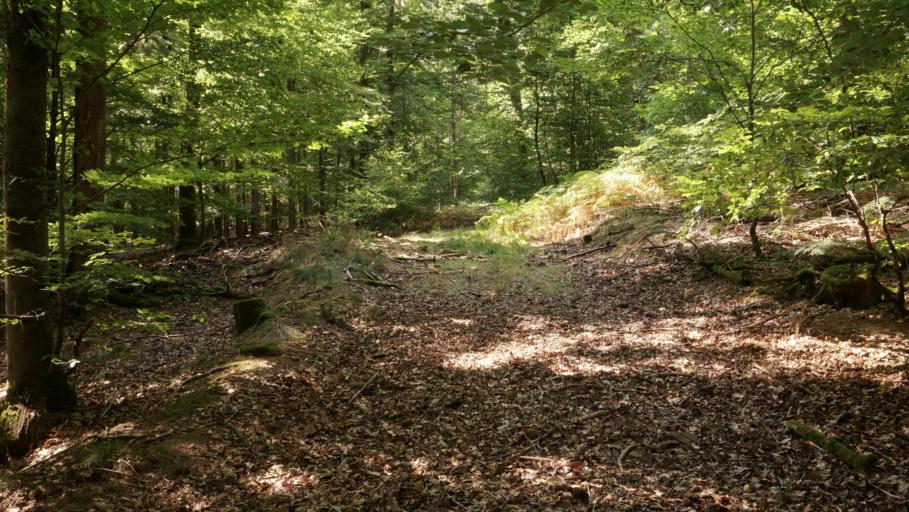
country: DE
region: Baden-Wuerttemberg
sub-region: Karlsruhe Region
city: Fahrenbach
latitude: 49.4431
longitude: 9.1443
